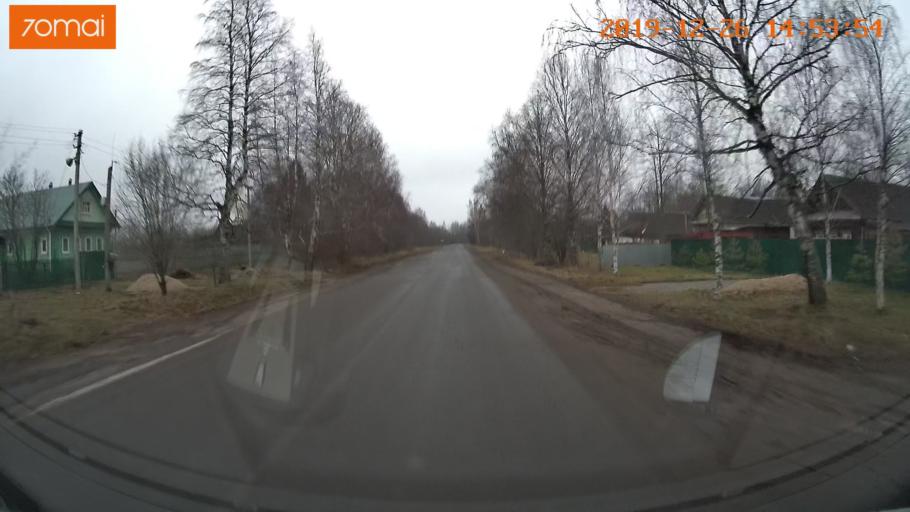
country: RU
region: Jaroslavl
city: Rybinsk
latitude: 58.3116
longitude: 38.8868
